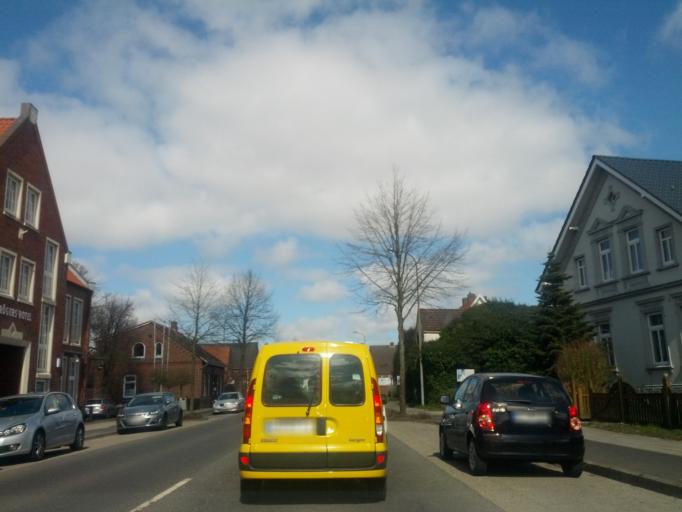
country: DE
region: Lower Saxony
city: Esens
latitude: 53.6406
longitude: 7.6126
